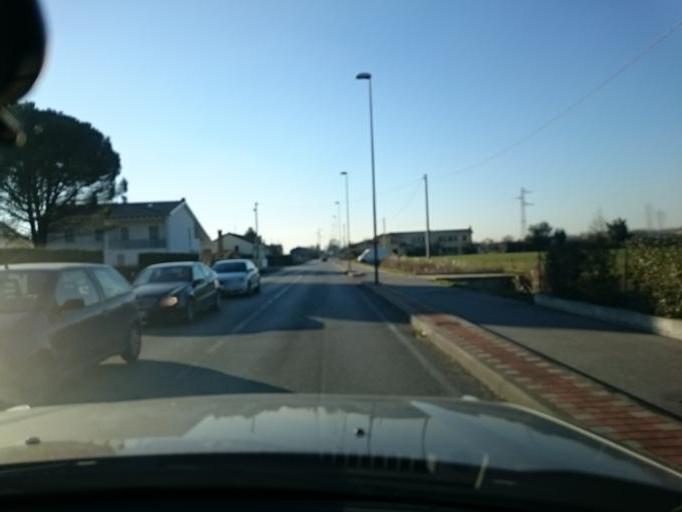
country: IT
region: Veneto
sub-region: Provincia di Venezia
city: Fosso
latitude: 45.4061
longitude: 12.0500
